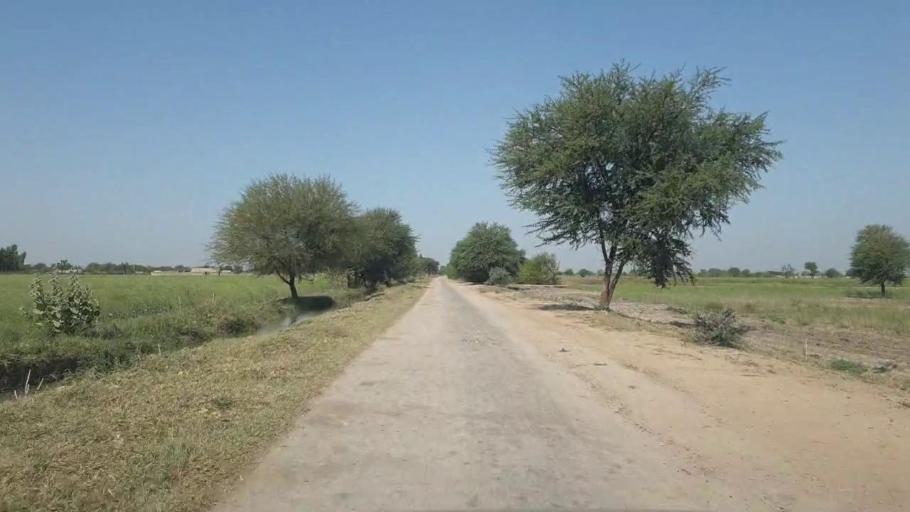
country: PK
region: Sindh
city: Umarkot
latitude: 25.2946
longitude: 69.6303
